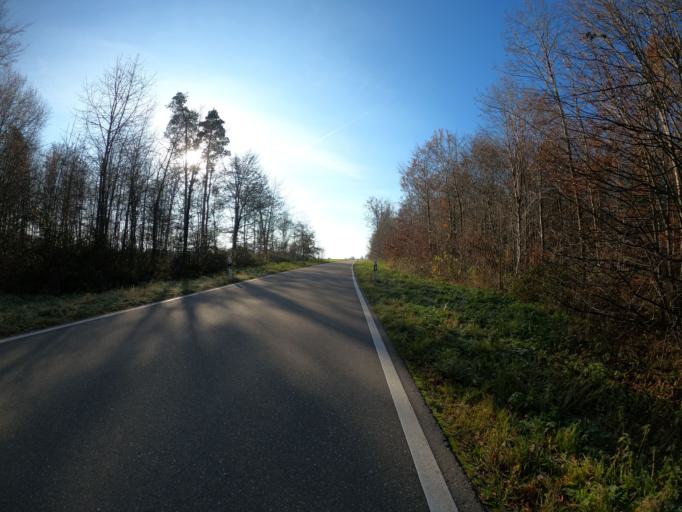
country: DE
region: Baden-Wuerttemberg
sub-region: Regierungsbezirk Stuttgart
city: Schlierbach
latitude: 48.6895
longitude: 9.5351
